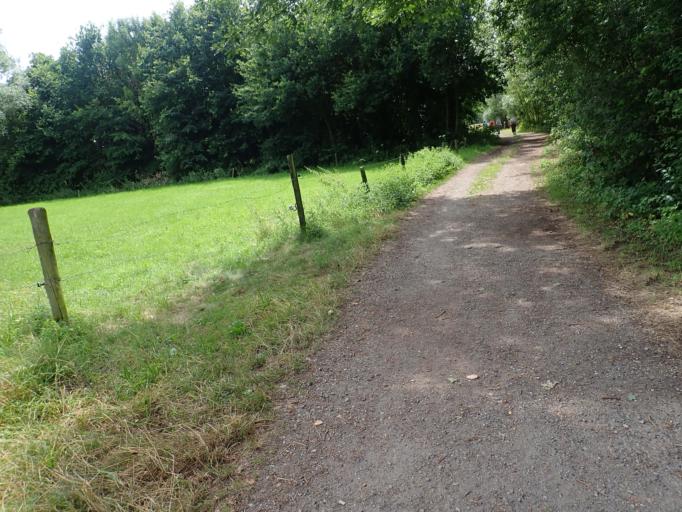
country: BE
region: Flanders
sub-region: Provincie Vlaams-Brabant
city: Keerbergen
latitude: 51.0003
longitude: 4.6227
